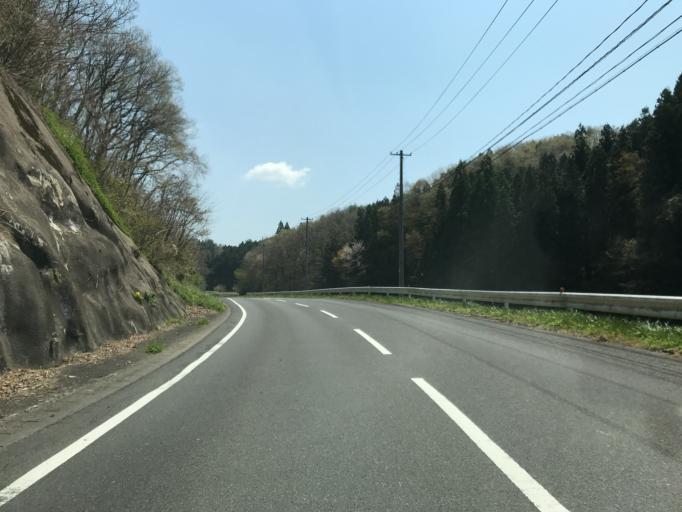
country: JP
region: Fukushima
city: Ishikawa
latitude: 37.0670
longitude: 140.4364
